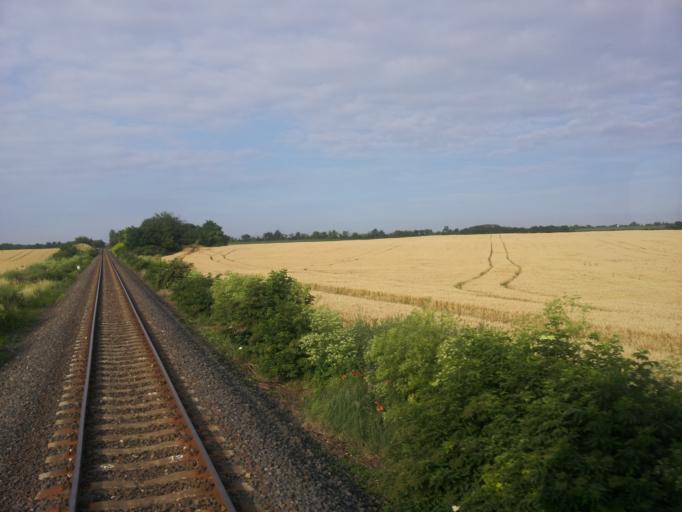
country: HU
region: Fejer
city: Polgardi
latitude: 47.0614
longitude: 18.2738
